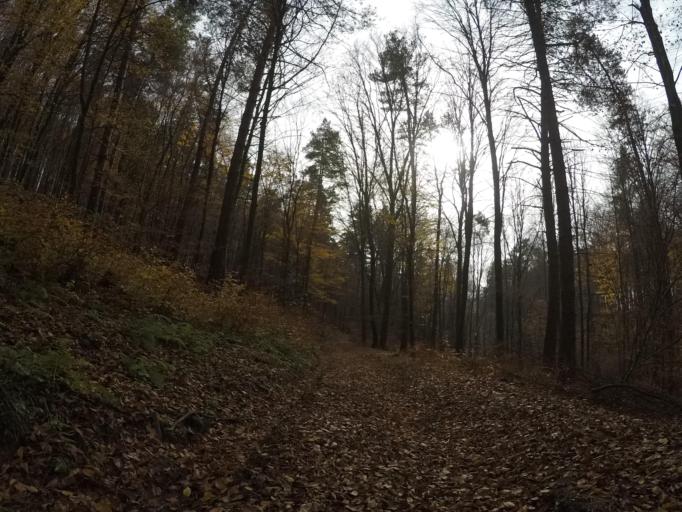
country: SK
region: Presovsky
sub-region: Okres Presov
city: Presov
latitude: 48.9495
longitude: 21.1831
